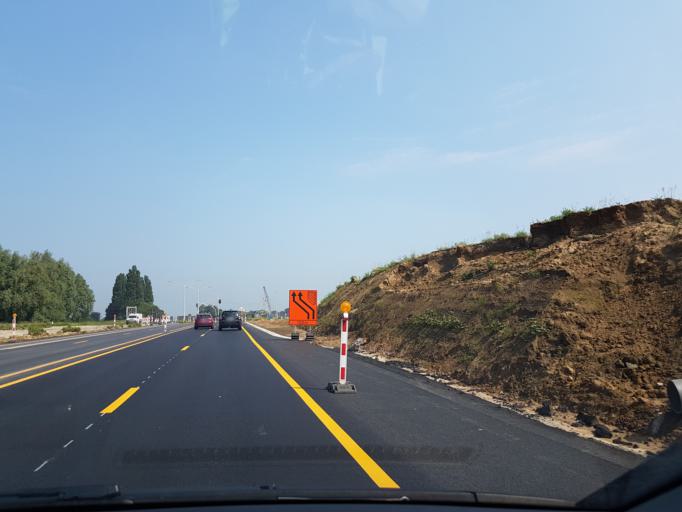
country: BE
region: Flanders
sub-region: Provincie Oost-Vlaanderen
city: Aalst
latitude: 50.9346
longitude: 4.0157
